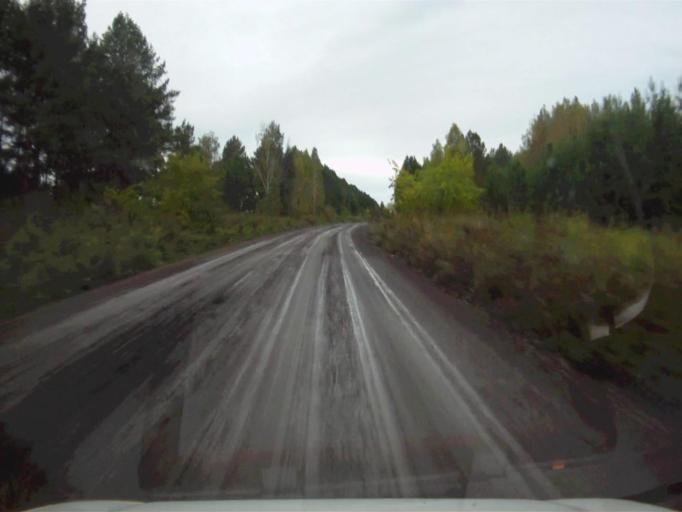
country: RU
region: Chelyabinsk
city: Nyazepetrovsk
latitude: 56.1402
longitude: 59.2952
